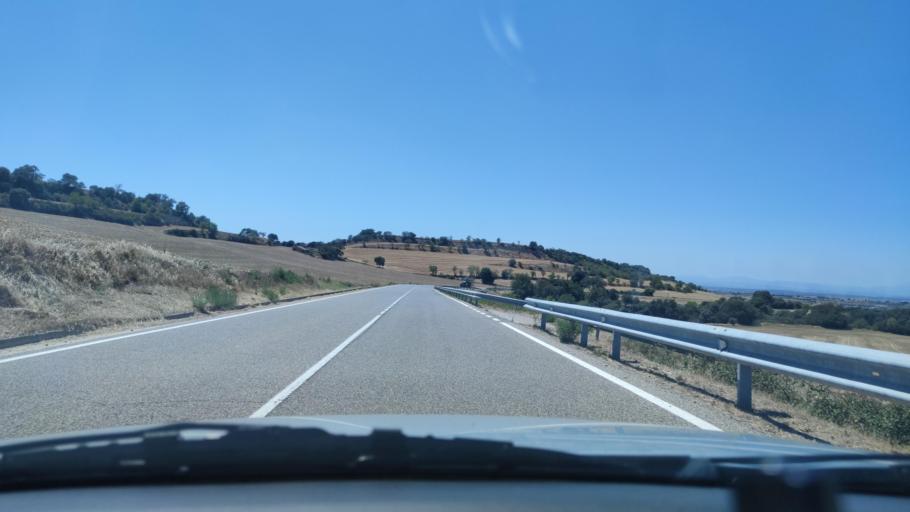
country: ES
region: Catalonia
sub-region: Provincia de Lleida
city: Ivorra
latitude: 41.7291
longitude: 1.3352
